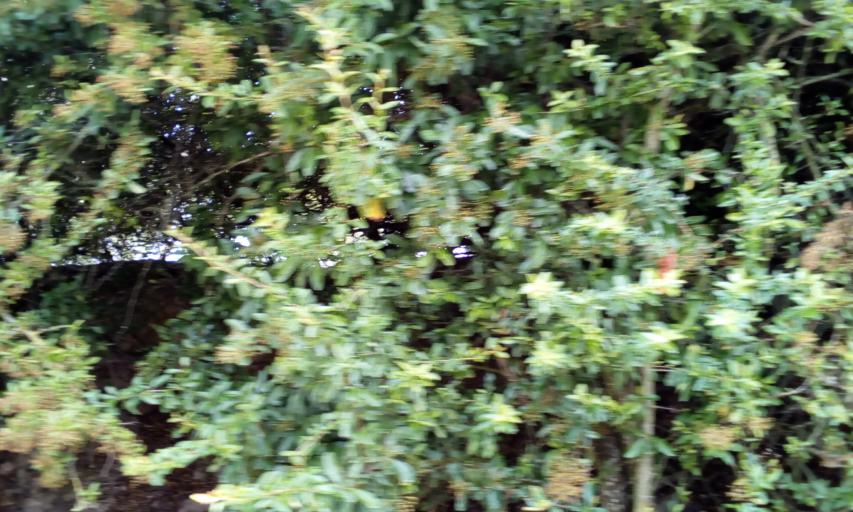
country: ES
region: La Rioja
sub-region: Provincia de La Rioja
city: Lardero
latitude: 42.4399
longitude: -2.5073
